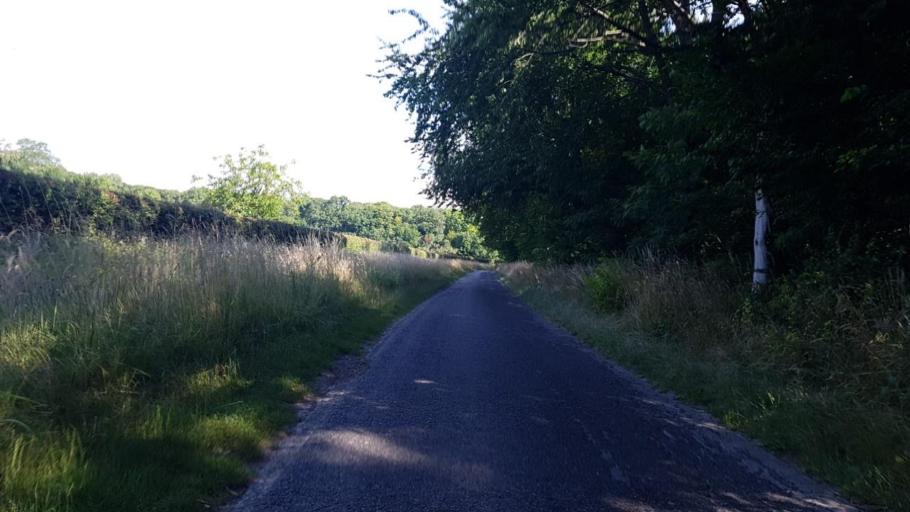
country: FR
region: Picardie
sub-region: Departement de l'Oise
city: Pontpoint
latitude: 49.2920
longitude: 2.6461
